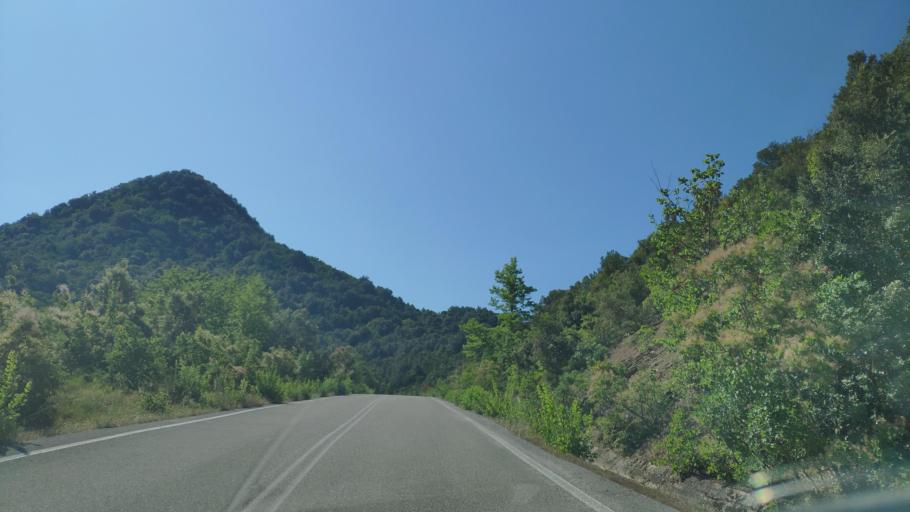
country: GR
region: West Greece
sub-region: Nomos Aitolias kai Akarnanias
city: Sardinia
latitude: 38.9222
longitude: 21.3912
